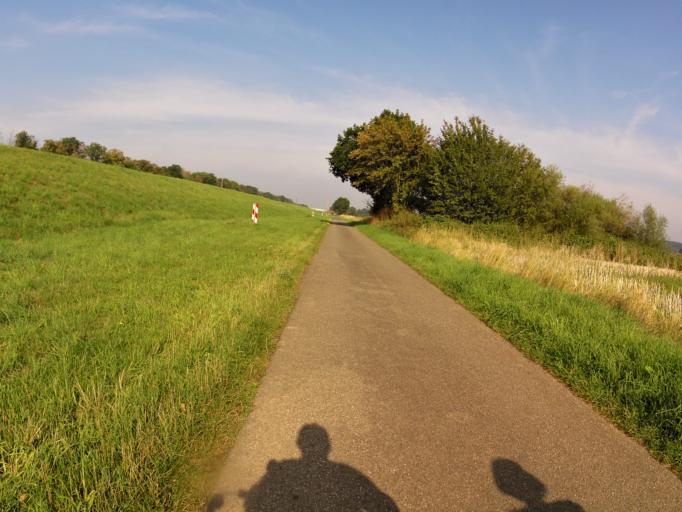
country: DE
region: Lower Saxony
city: Langwedel
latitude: 52.9650
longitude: 9.1682
